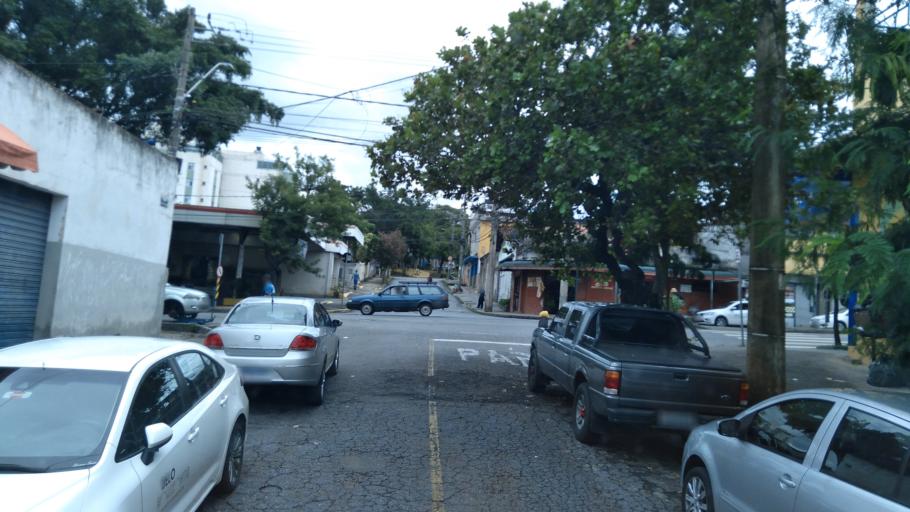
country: BR
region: Minas Gerais
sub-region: Belo Horizonte
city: Belo Horizonte
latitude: -19.8964
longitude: -43.9063
